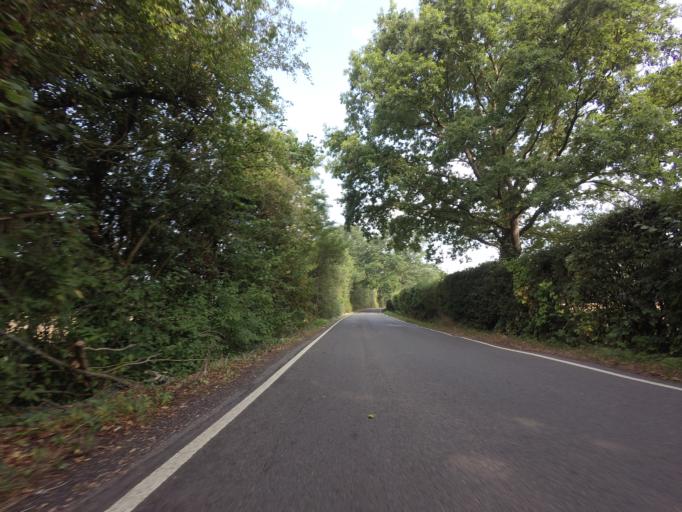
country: GB
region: England
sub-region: Kent
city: Tenterden
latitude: 51.1148
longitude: 0.6816
